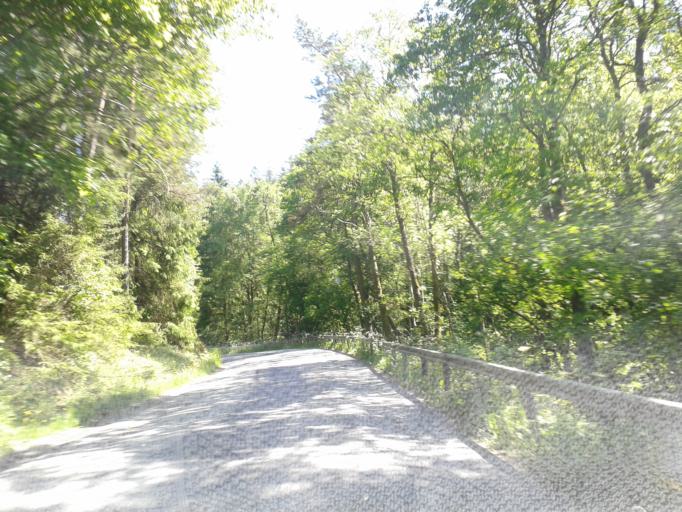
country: SE
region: Vaestra Goetaland
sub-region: Stenungsunds Kommun
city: Stora Hoga
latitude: 58.0173
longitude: 11.9009
